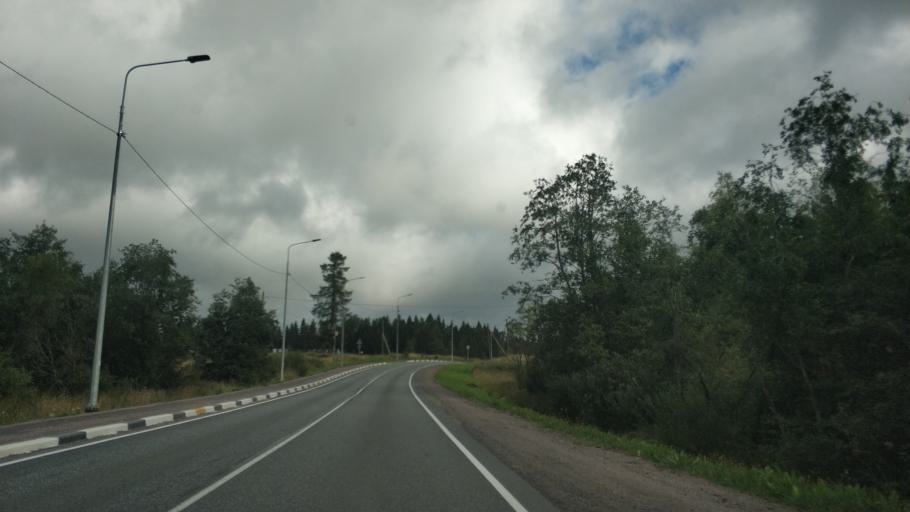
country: RU
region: Republic of Karelia
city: Khelyulya
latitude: 61.7667
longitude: 30.6544
